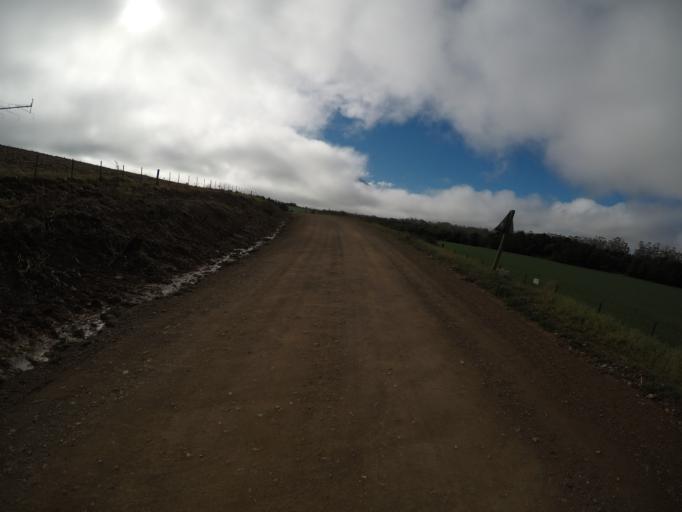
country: ZA
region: Western Cape
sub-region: Overberg District Municipality
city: Caledon
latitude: -34.1163
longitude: 19.7894
